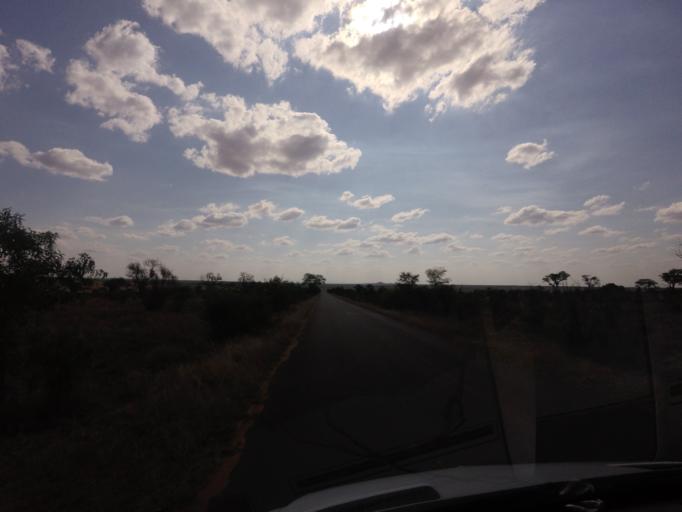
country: ZA
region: Limpopo
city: Thulamahashi
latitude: -24.3936
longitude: 31.6016
